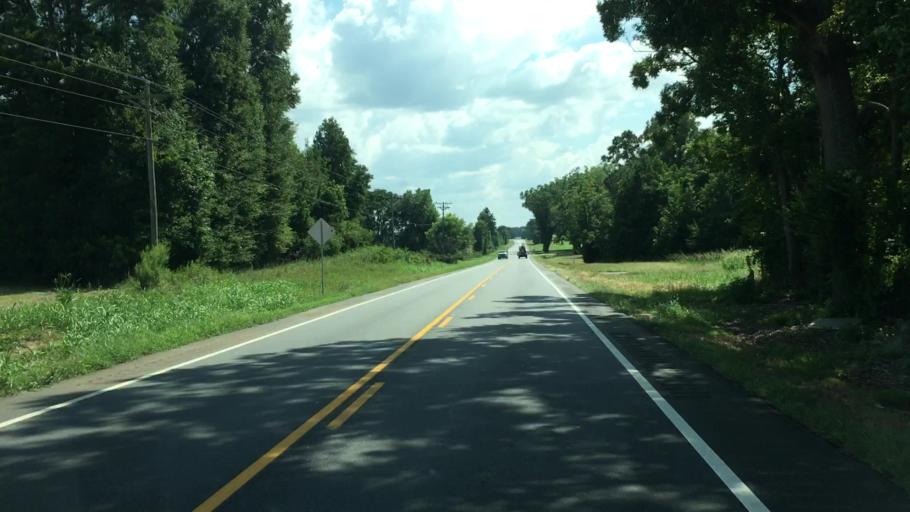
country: US
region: Georgia
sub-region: Morgan County
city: Madison
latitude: 33.5199
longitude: -83.4450
